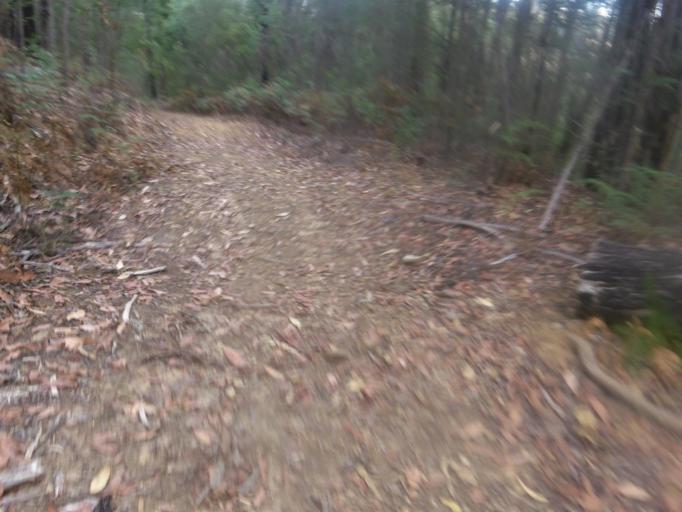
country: AU
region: Victoria
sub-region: Murrindindi
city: Alexandra
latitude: -37.3832
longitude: 145.5520
